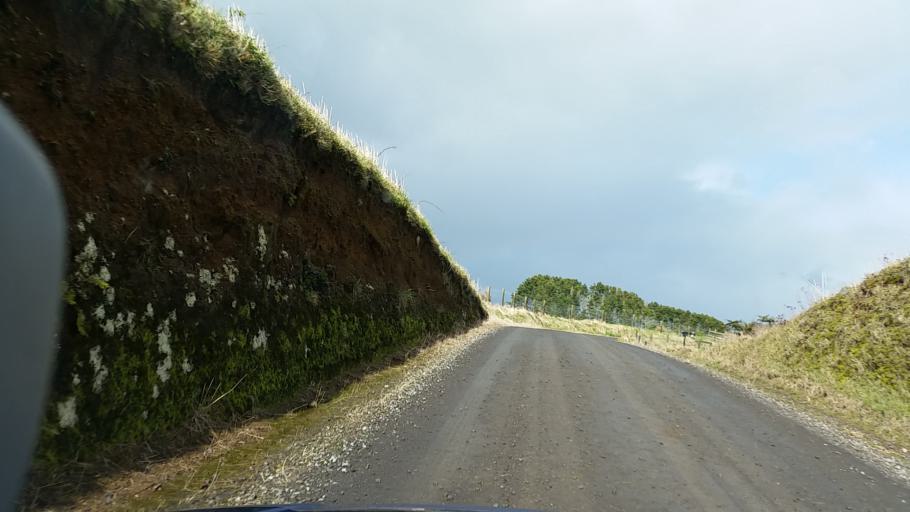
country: NZ
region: Taranaki
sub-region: South Taranaki District
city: Eltham
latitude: -39.2793
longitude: 174.3082
